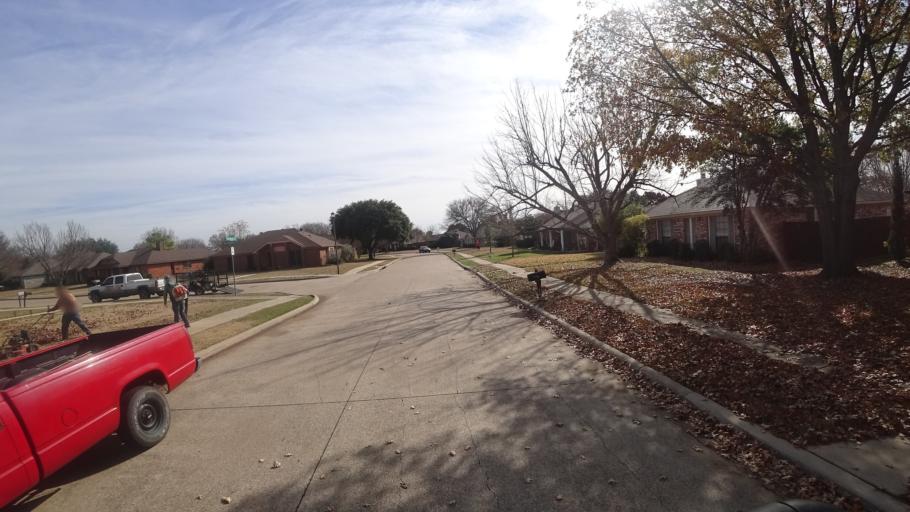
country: US
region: Texas
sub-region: Denton County
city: Highland Village
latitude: 33.0595
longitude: -97.0391
